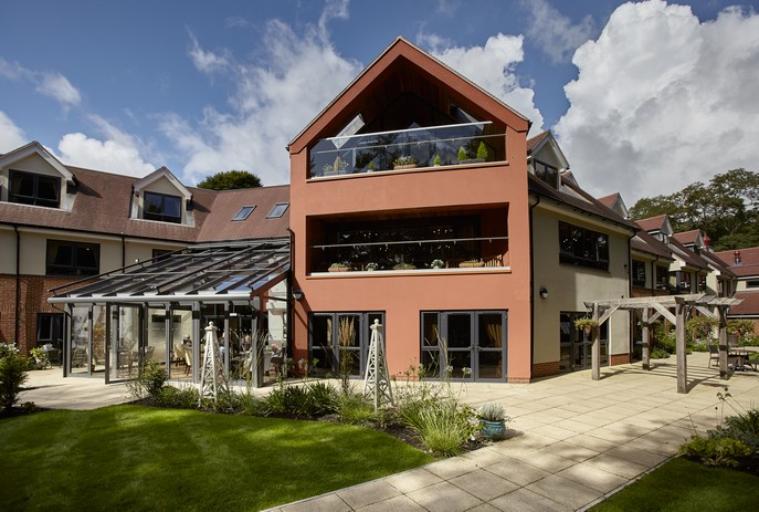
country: GB
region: England
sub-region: Surrey
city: Byfleet
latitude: 51.3382
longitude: -0.4512
